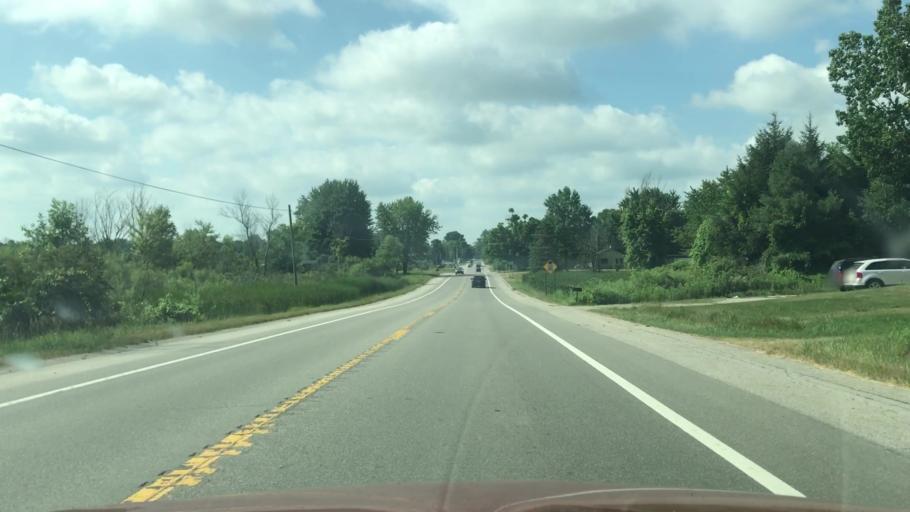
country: US
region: Michigan
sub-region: Kent County
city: Kent City
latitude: 43.2857
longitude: -85.8104
